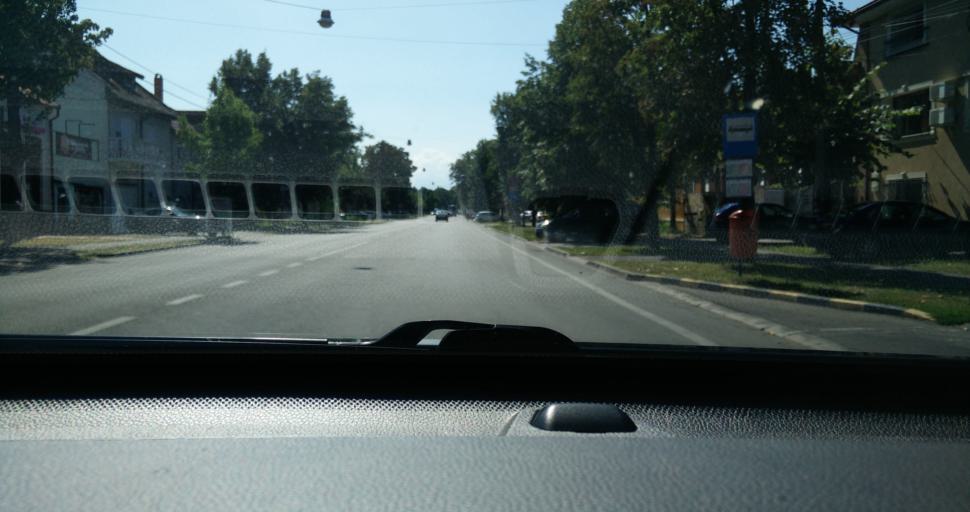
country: RO
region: Bihor
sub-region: Comuna Biharea
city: Oradea
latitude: 47.0487
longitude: 21.9299
